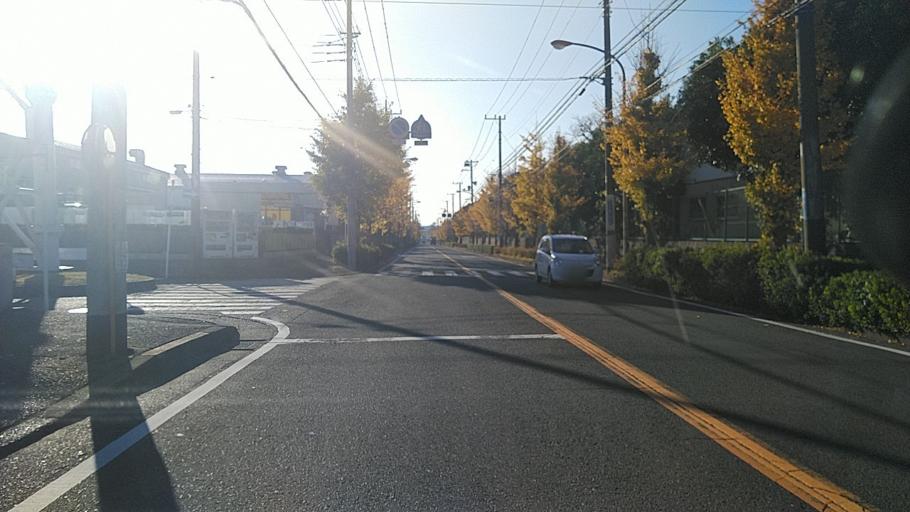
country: JP
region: Kanagawa
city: Fujisawa
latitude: 35.3808
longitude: 139.4486
